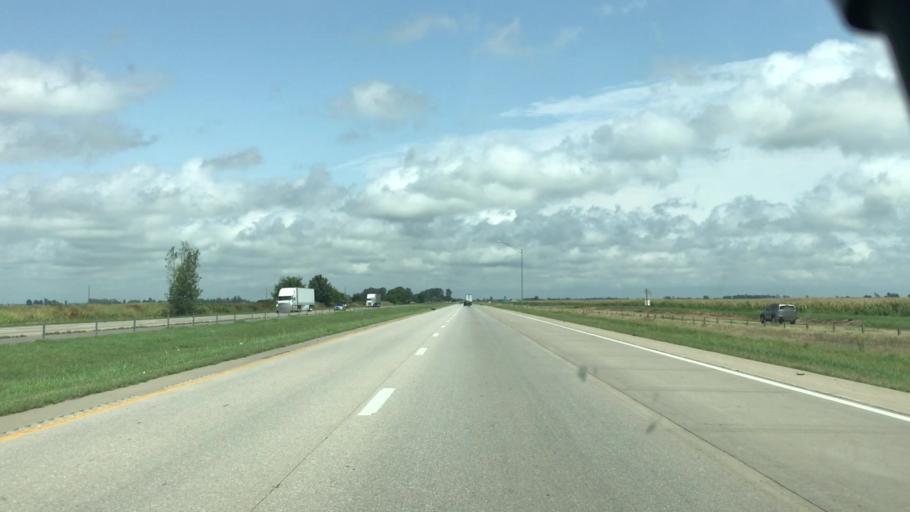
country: US
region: Missouri
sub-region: Pemiscot County
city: Steele
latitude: 36.1118
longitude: -89.7692
